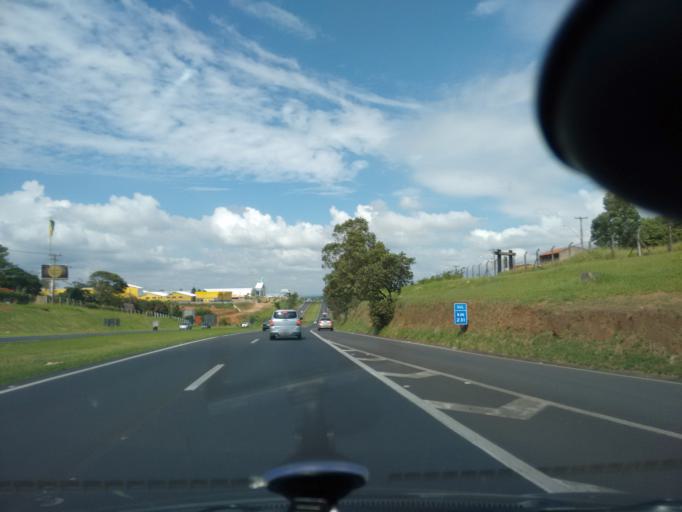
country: BR
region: Sao Paulo
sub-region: Sao Carlos
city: Sao Carlos
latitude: -22.0167
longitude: -47.8575
